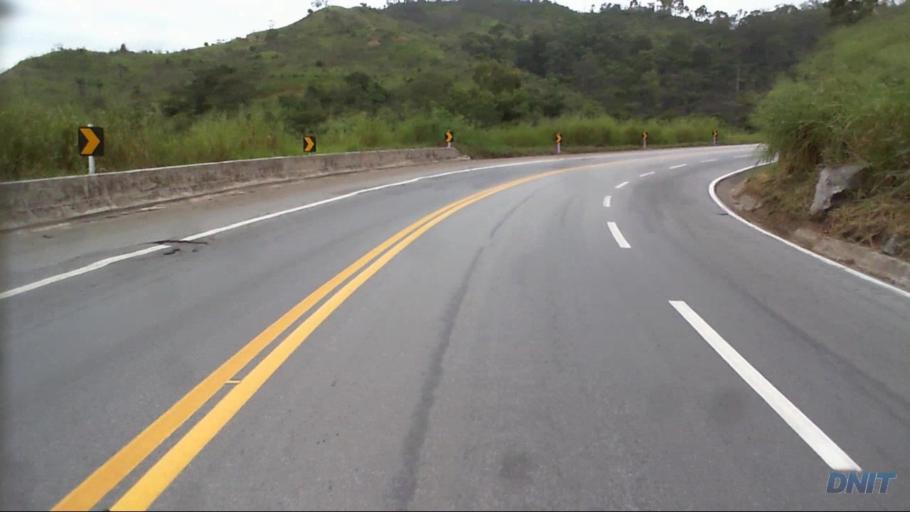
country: BR
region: Minas Gerais
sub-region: Timoteo
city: Timoteo
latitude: -19.6398
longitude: -42.8169
